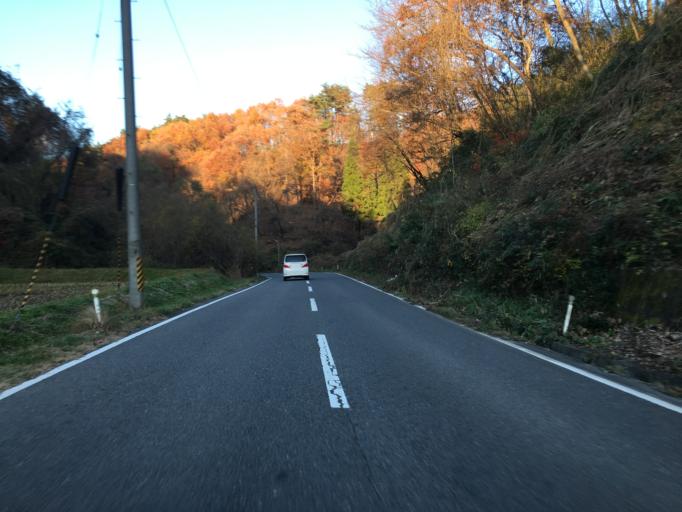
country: JP
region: Fukushima
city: Motomiya
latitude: 37.5232
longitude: 140.4596
